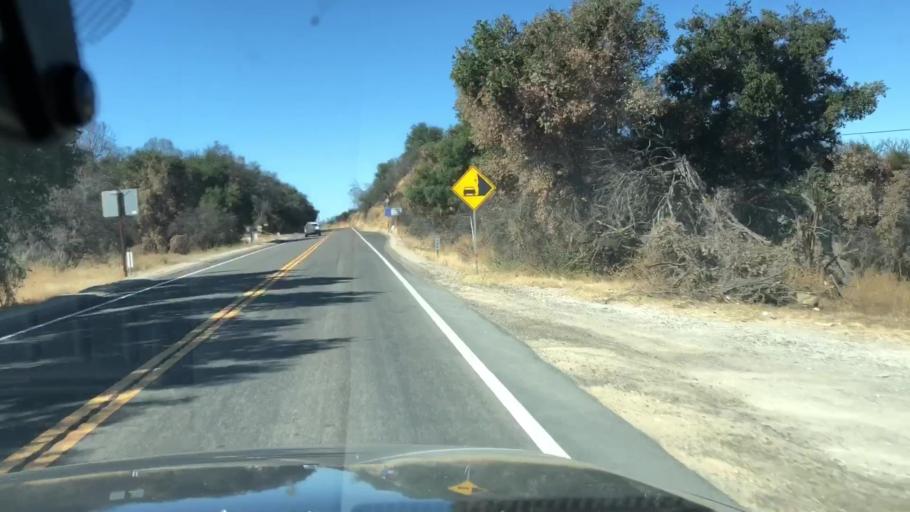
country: US
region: California
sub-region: Santa Barbara County
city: Santa Ynez
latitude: 34.5663
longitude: -119.9400
